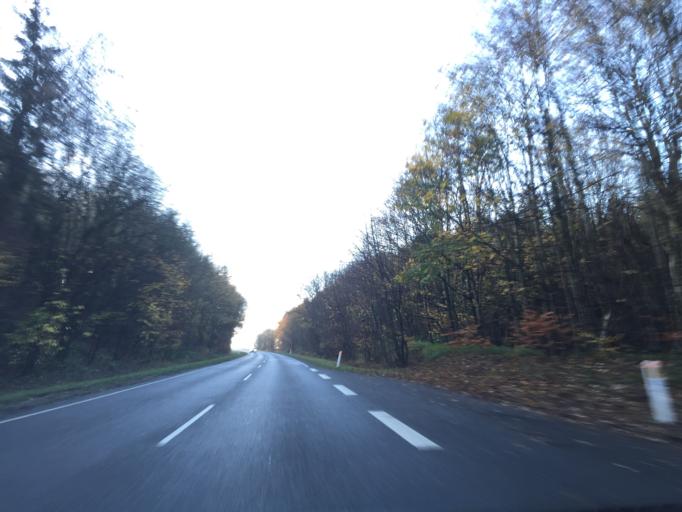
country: DK
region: Central Jutland
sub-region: Arhus Kommune
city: Framlev
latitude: 56.1868
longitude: 9.9896
